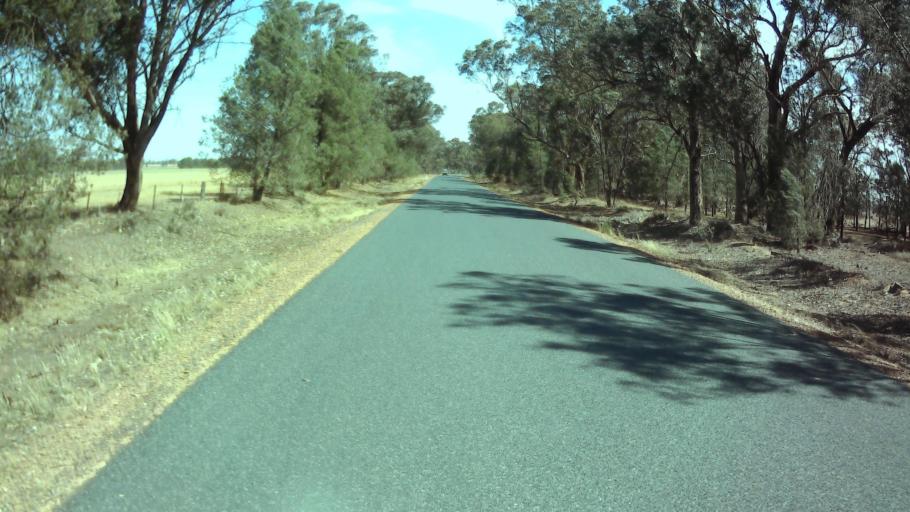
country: AU
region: New South Wales
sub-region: Weddin
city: Grenfell
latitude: -34.0345
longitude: 148.1341
